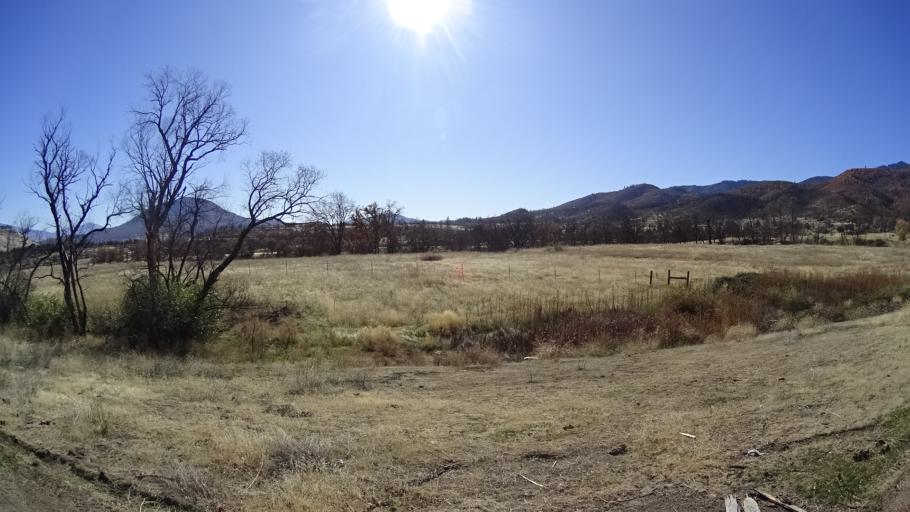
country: US
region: California
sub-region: Siskiyou County
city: Yreka
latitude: 41.9193
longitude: -122.5765
